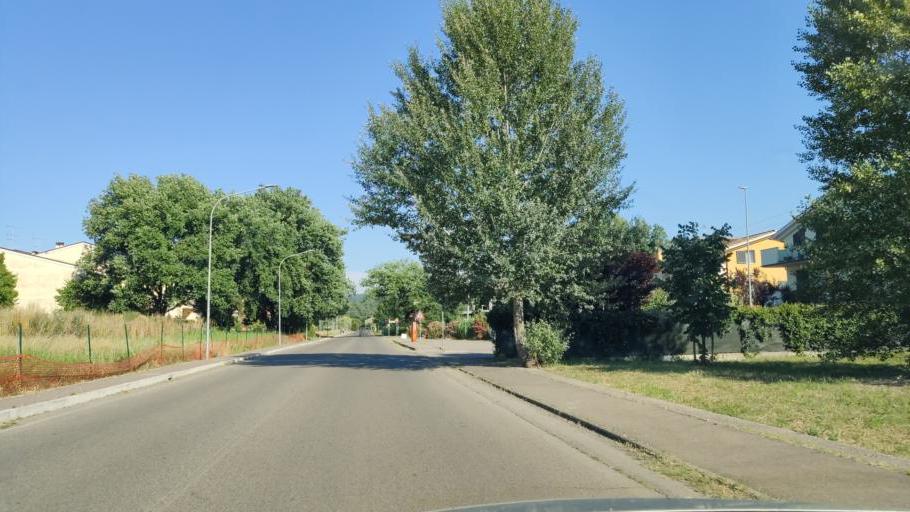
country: IT
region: Latium
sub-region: Provincia di Viterbo
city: Orte
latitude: 42.4676
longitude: 12.3903
